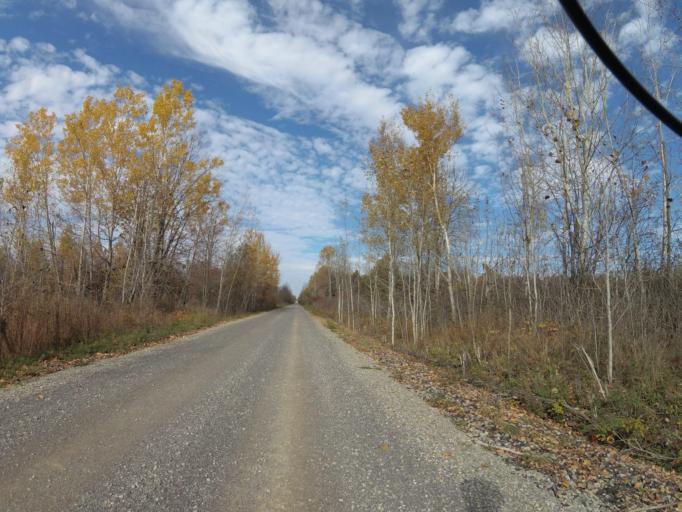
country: CA
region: Ontario
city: Carleton Place
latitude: 45.0518
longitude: -76.0898
